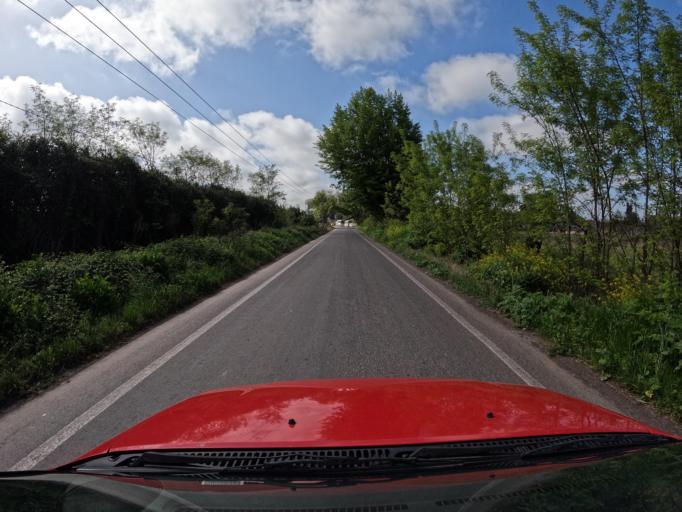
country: CL
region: Maule
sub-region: Provincia de Curico
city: Teno
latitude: -34.8821
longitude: -71.2289
